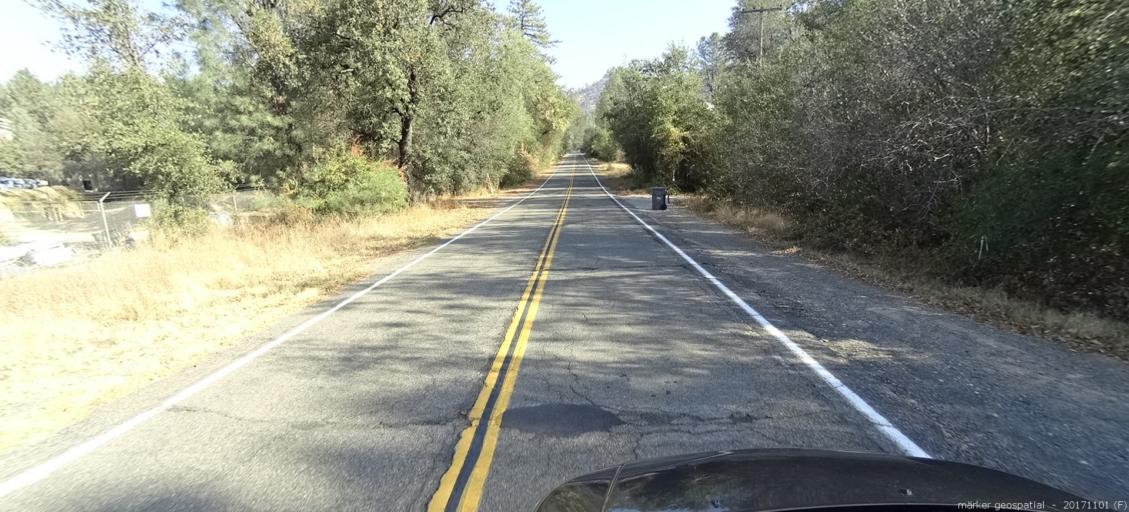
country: US
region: California
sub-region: Shasta County
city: Shasta Lake
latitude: 40.7355
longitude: -122.3202
